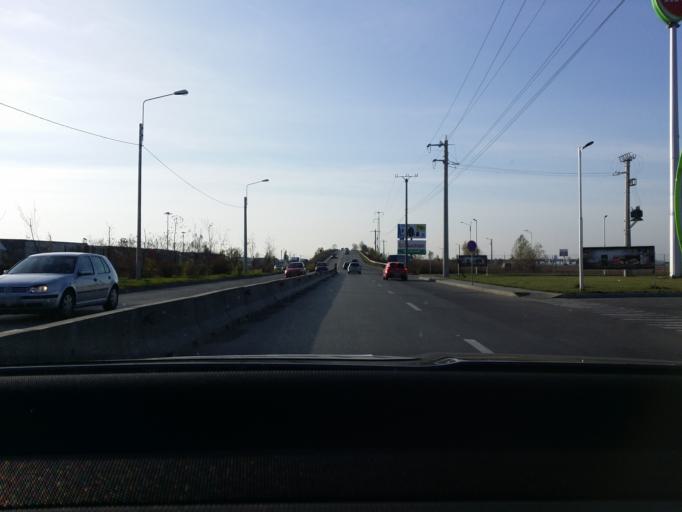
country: RO
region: Prahova
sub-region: Comuna Targsoru Vechi
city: Strejnicu
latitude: 44.9398
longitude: 25.9728
